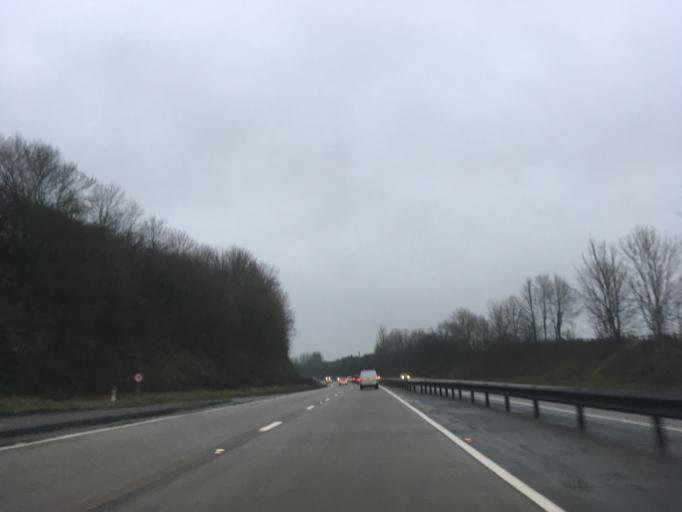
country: GB
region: Wales
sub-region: Cardiff
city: Pentyrch
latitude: 51.4953
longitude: -3.2952
